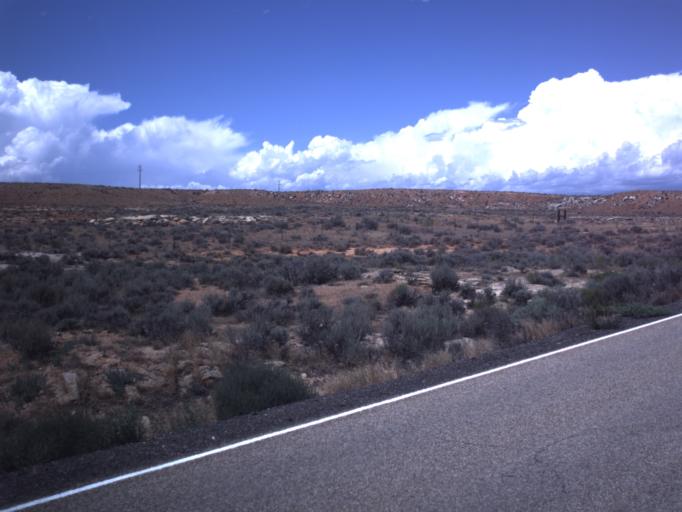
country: US
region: Utah
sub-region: Uintah County
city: Maeser
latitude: 40.2753
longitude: -109.6818
